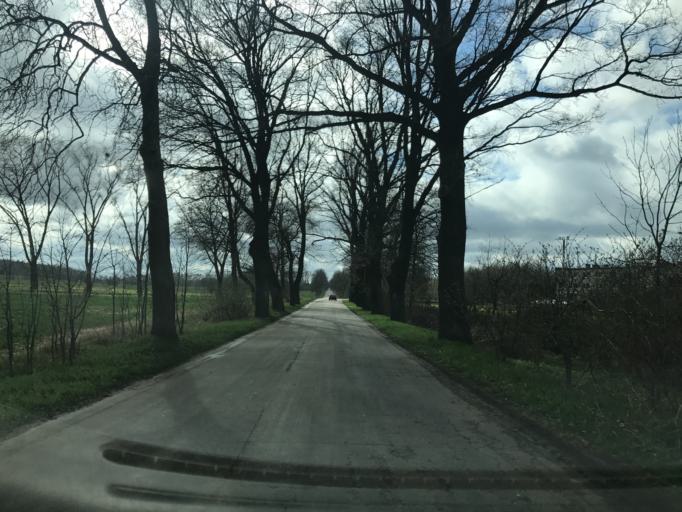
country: PL
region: Warmian-Masurian Voivodeship
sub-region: Powiat ostrodzki
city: Gierzwald
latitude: 53.4841
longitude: 20.0974
